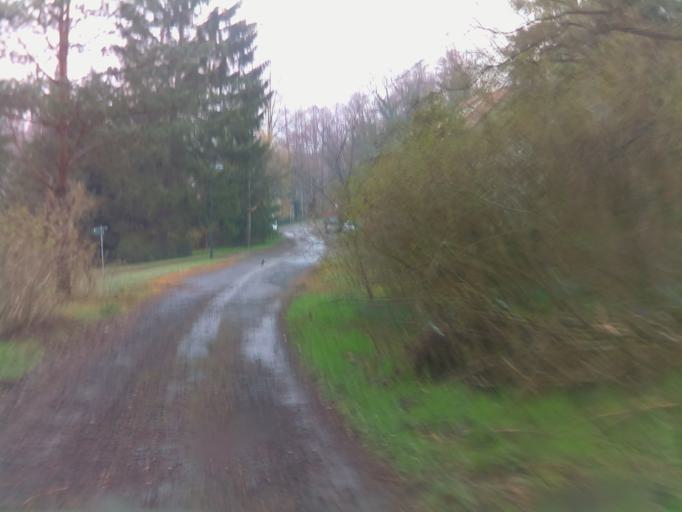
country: DE
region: Brandenburg
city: Jamlitz
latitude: 51.9860
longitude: 14.3621
